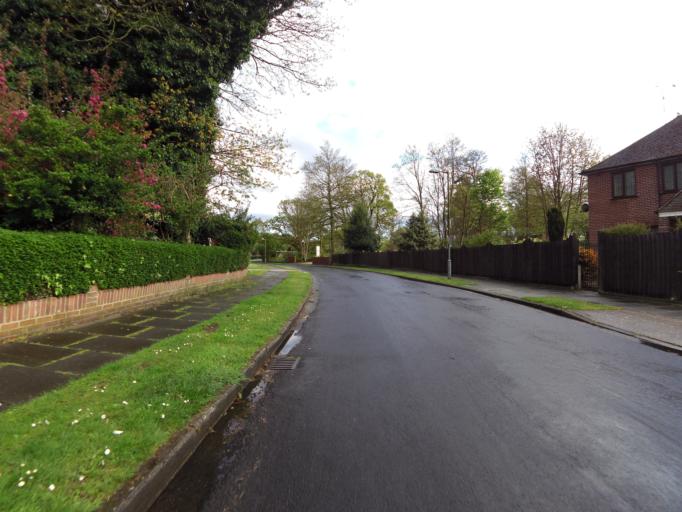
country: GB
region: England
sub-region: Suffolk
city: Kesgrave
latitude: 52.0436
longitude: 1.1978
